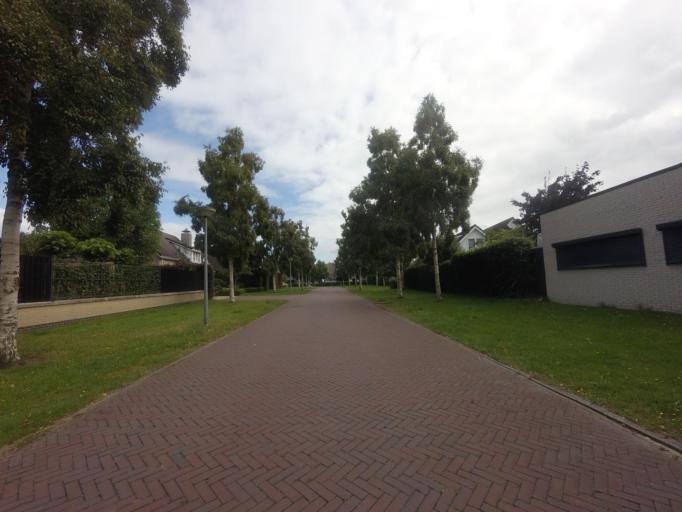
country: NL
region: North Holland
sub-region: Gemeente Huizen
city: Huizen
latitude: 52.2954
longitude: 5.2818
